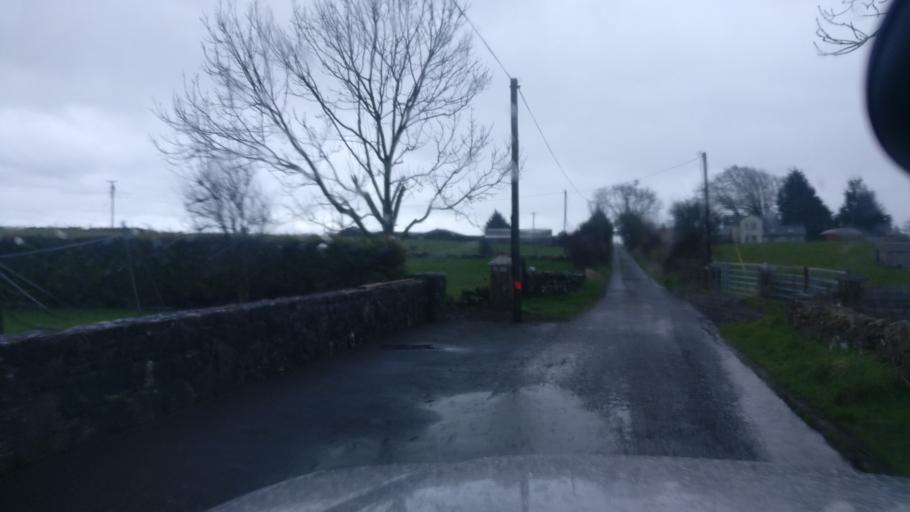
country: IE
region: Connaught
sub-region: County Galway
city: Loughrea
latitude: 53.2413
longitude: -8.4236
